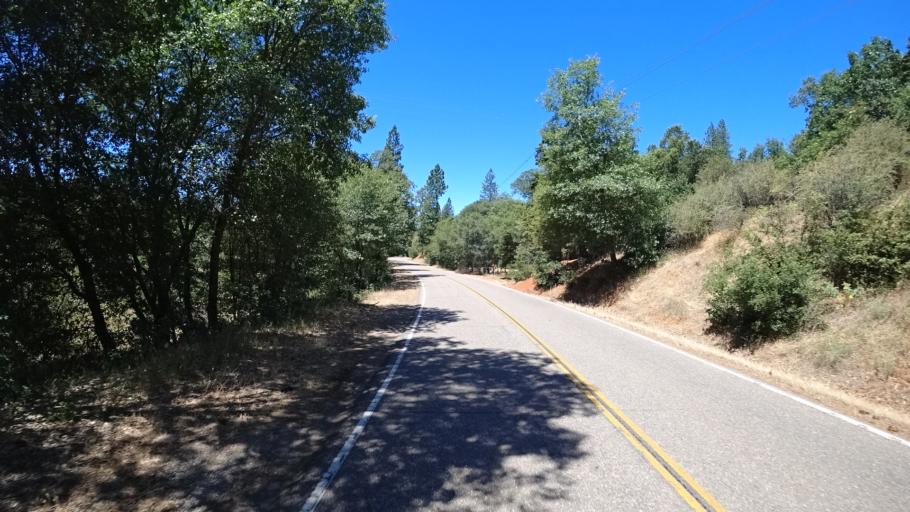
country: US
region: California
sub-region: Amador County
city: Pioneer
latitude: 38.3798
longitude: -120.5176
